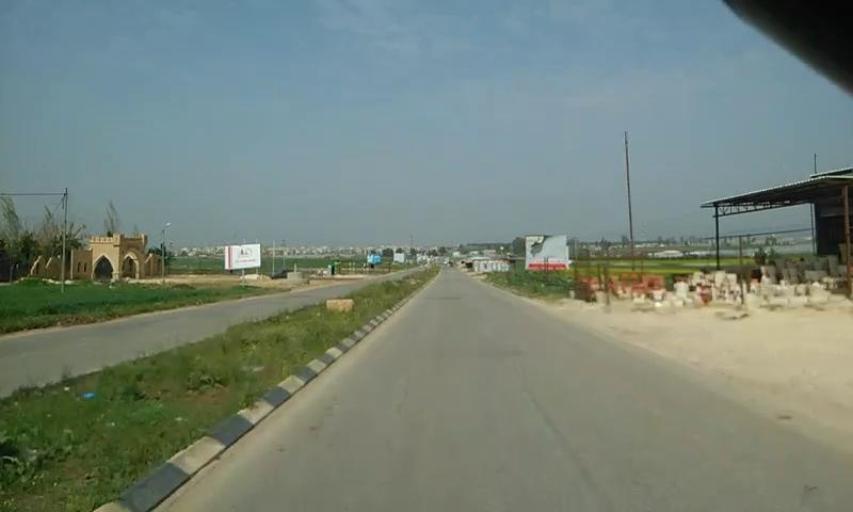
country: PS
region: West Bank
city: Al Jalamah
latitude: 32.4977
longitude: 35.3020
